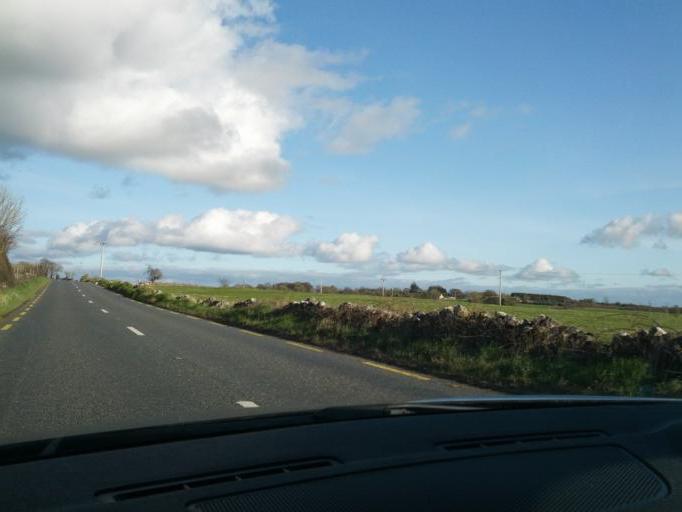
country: IE
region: Connaught
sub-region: Roscommon
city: Roscommon
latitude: 53.6676
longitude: -8.3131
